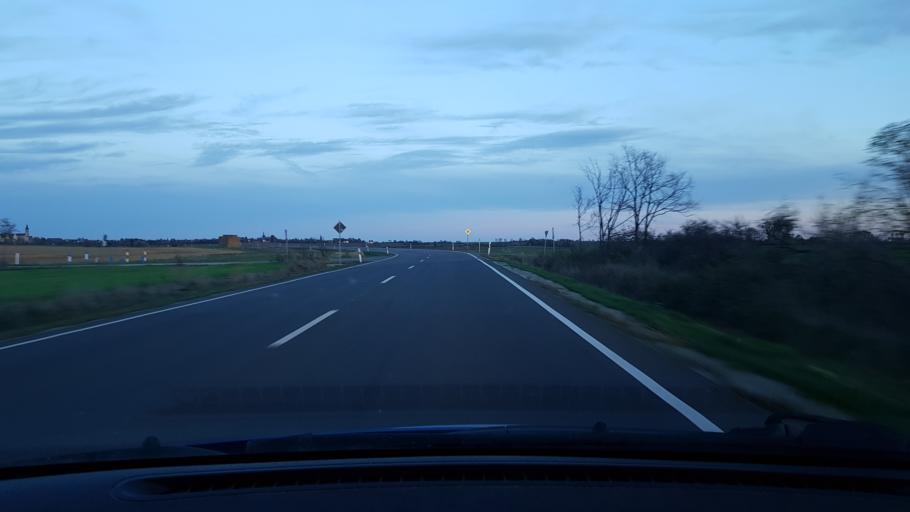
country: DE
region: Saxony-Anhalt
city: Leitzkau
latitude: 52.0605
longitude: 11.9184
